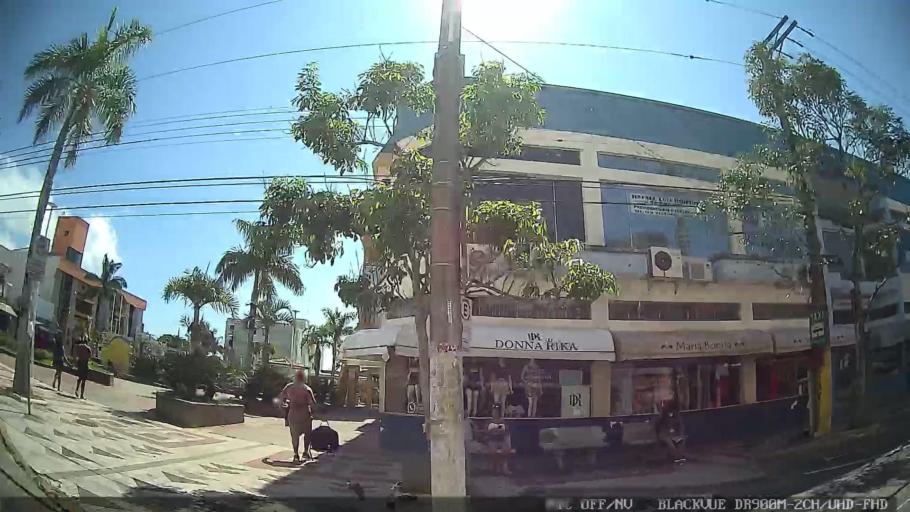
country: BR
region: Sao Paulo
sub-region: Peruibe
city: Peruibe
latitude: -24.3219
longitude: -46.9976
